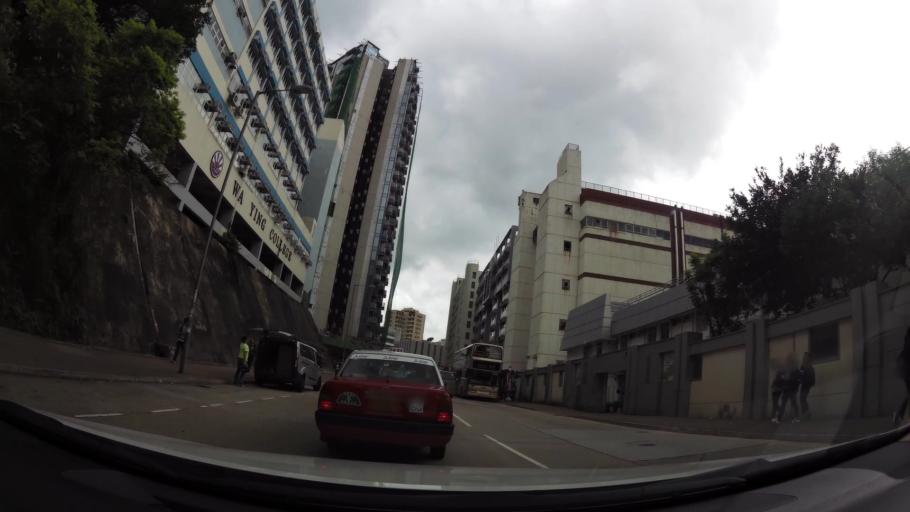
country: HK
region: Kowloon City
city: Kowloon
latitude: 22.3200
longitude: 114.1828
